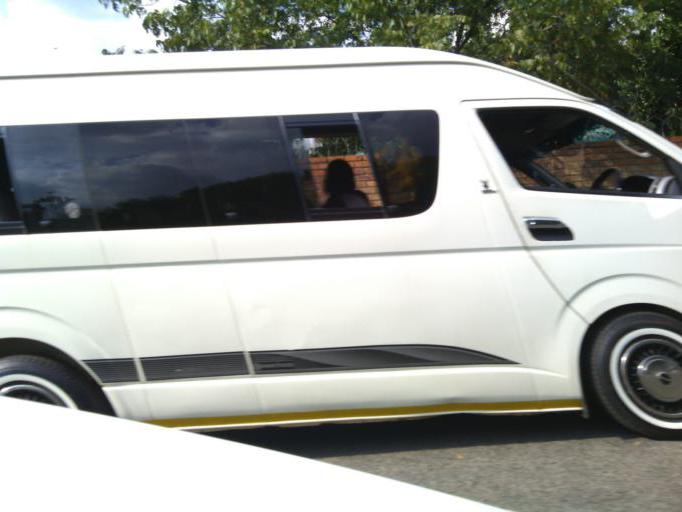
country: ZA
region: Gauteng
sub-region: City of Tshwane Metropolitan Municipality
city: Centurion
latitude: -25.8343
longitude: 28.2014
